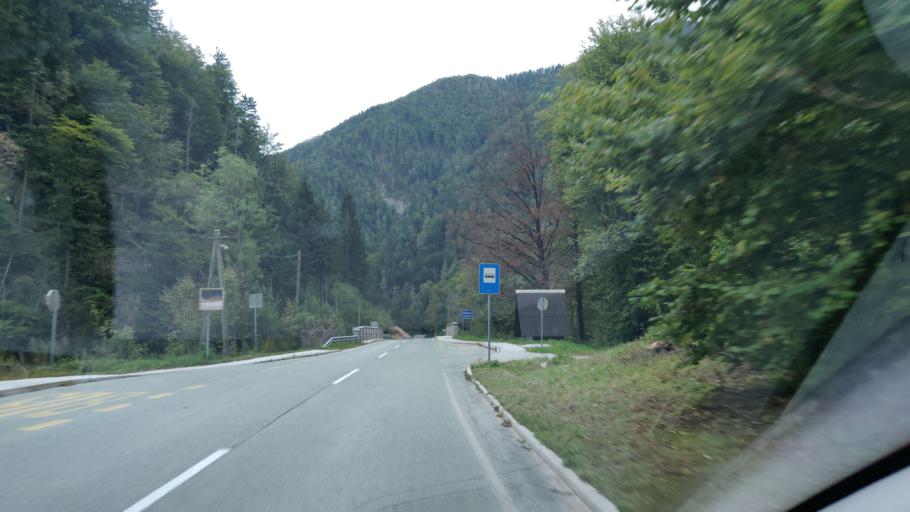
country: SI
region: Jezersko
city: Zgornje Jezersko
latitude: 46.3586
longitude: 14.4712
